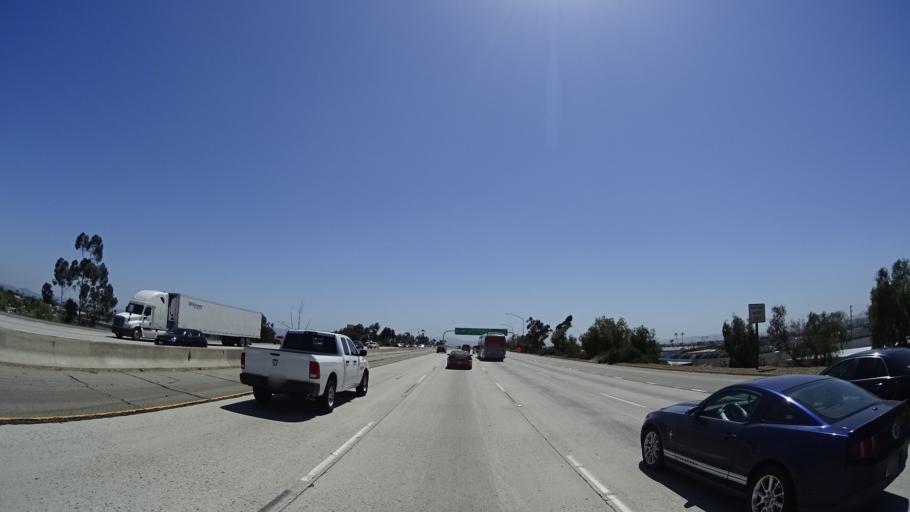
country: US
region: California
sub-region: Los Angeles County
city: San Fernando
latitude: 34.2748
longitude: -118.4259
